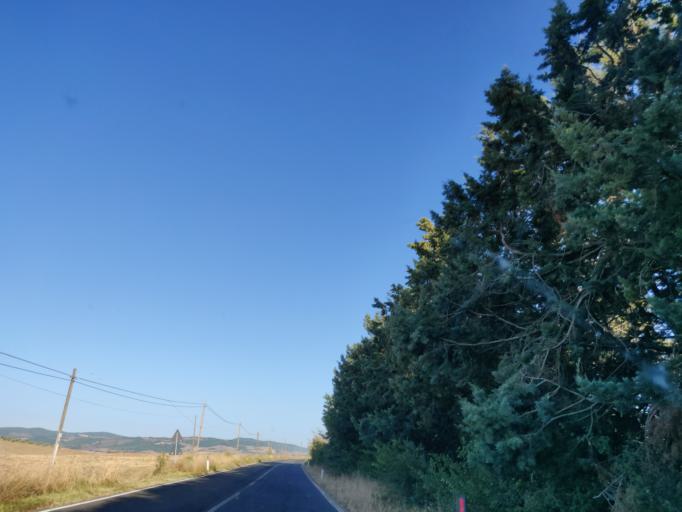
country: IT
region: Tuscany
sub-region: Provincia di Siena
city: Piancastagnaio
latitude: 42.8184
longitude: 11.7362
